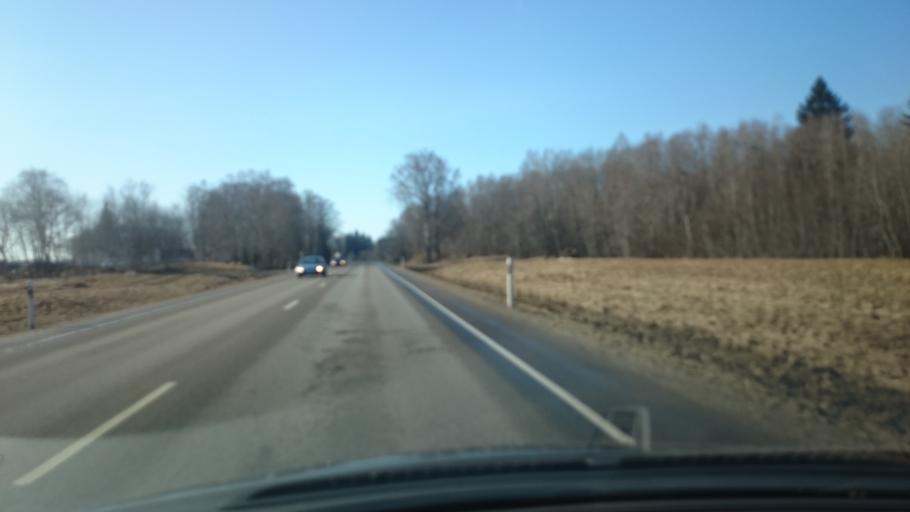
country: EE
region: Raplamaa
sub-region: Kohila vald
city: Kohila
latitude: 59.2588
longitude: 24.7409
